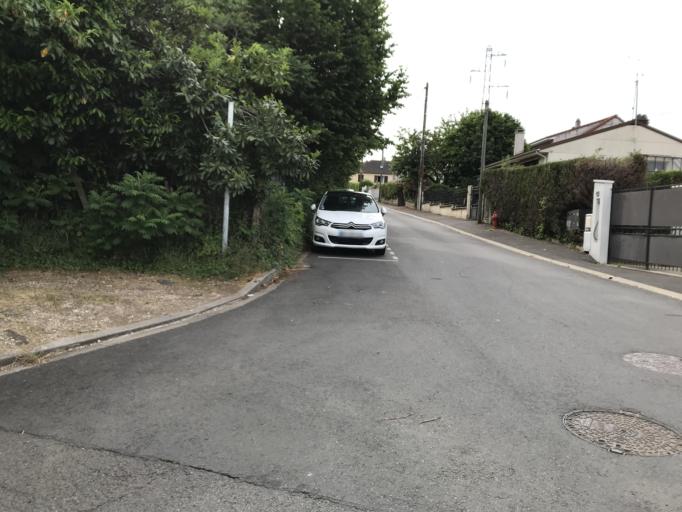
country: FR
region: Ile-de-France
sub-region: Departement de l'Essonne
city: Longpont-sur-Orge
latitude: 48.6323
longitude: 2.2913
